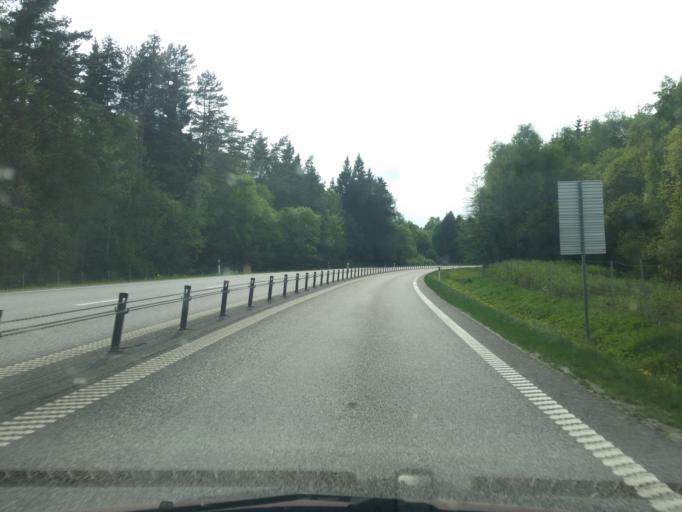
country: SE
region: Vaestra Goetaland
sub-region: Ulricehamns Kommun
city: Ulricehamn
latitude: 57.8016
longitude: 13.3631
